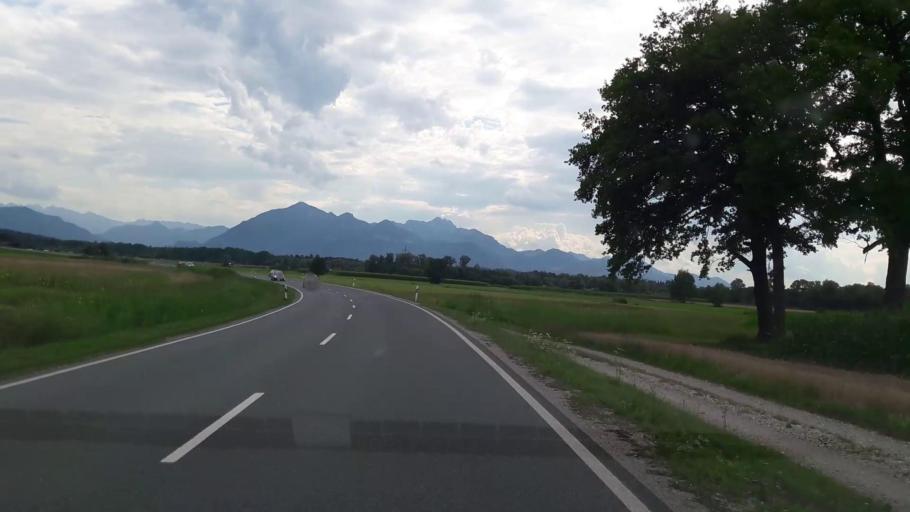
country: DE
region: Bavaria
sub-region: Upper Bavaria
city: Grabenstatt
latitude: 47.8368
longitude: 12.5255
